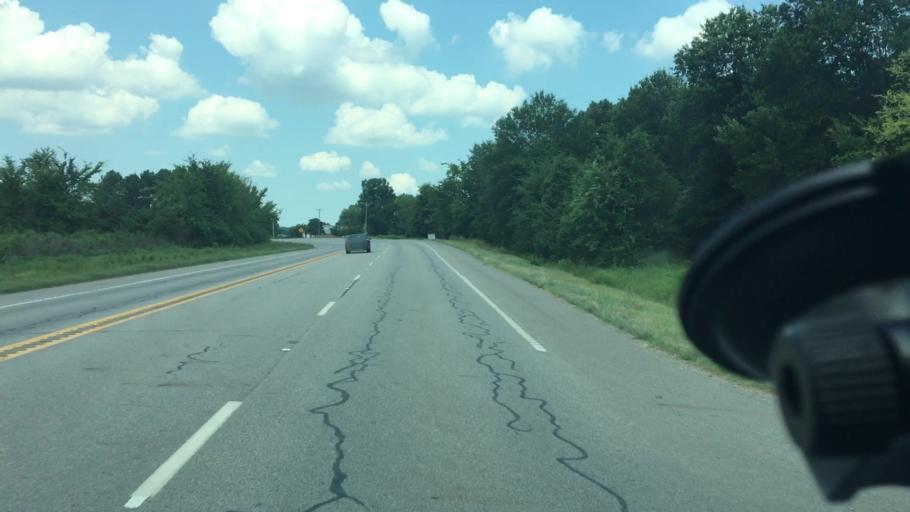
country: US
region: Arkansas
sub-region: Logan County
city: Paris
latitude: 35.2979
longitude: -93.8110
